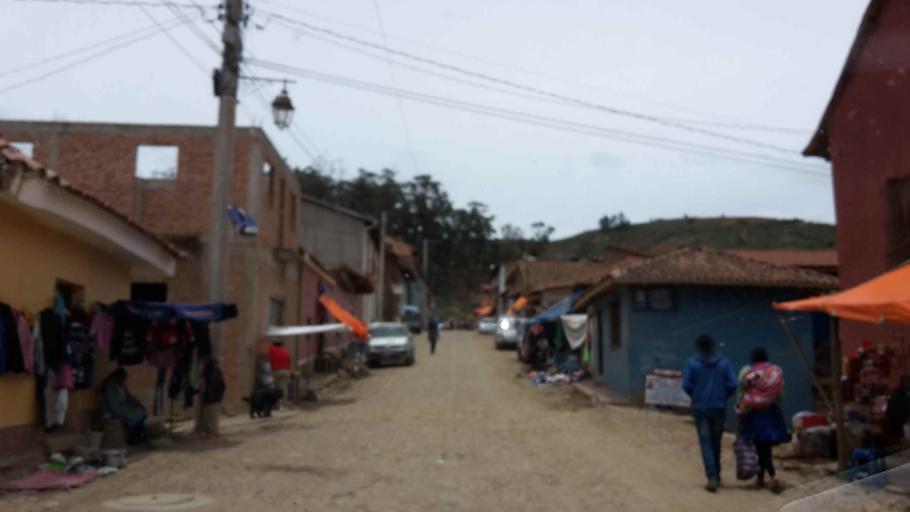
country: BO
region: Cochabamba
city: Totora
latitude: -17.7363
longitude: -65.1923
